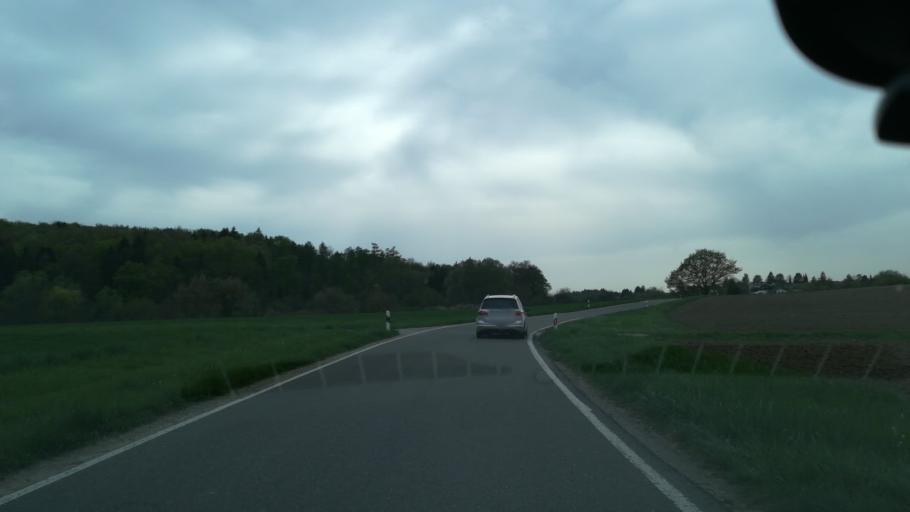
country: DE
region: Baden-Wuerttemberg
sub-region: Tuebingen Region
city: Uberlingen
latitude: 47.7352
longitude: 9.1309
